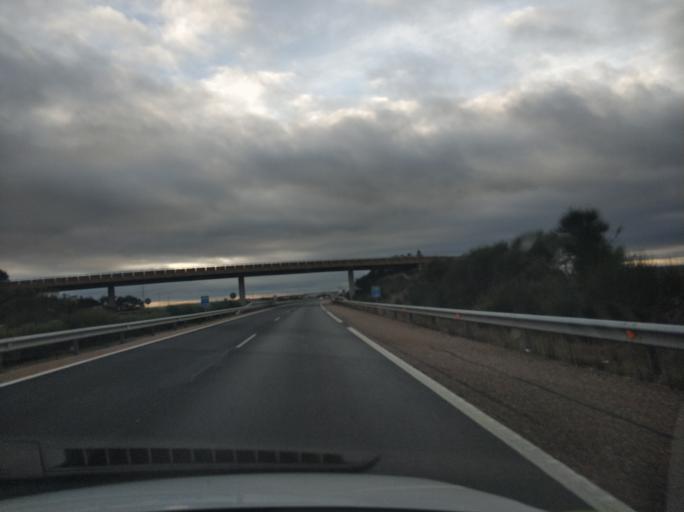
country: ES
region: Castille and Leon
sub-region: Provincia de Salamanca
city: Castellanos de Moriscos
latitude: 41.0346
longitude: -5.5658
